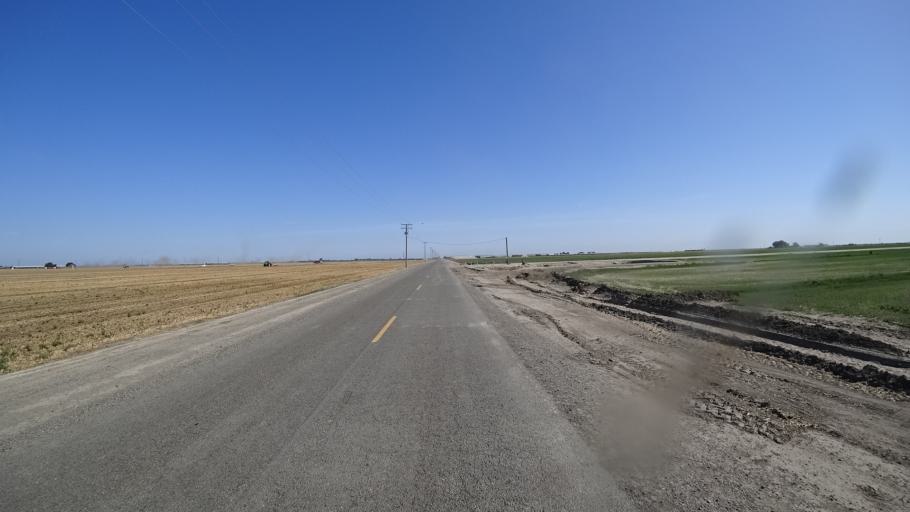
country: US
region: California
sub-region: Kings County
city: Home Garden
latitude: 36.2301
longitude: -119.5562
